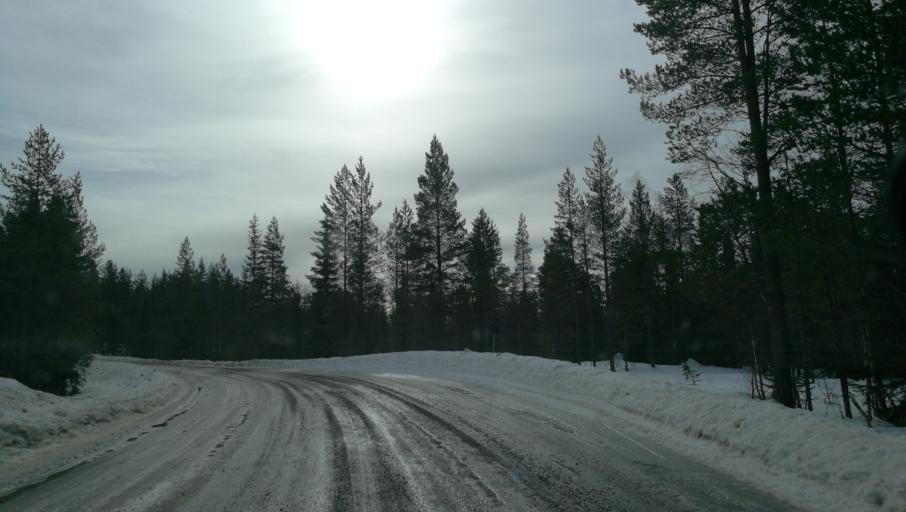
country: SE
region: Vaermland
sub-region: Torsby Kommun
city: Torsby
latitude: 60.6504
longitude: 12.8933
